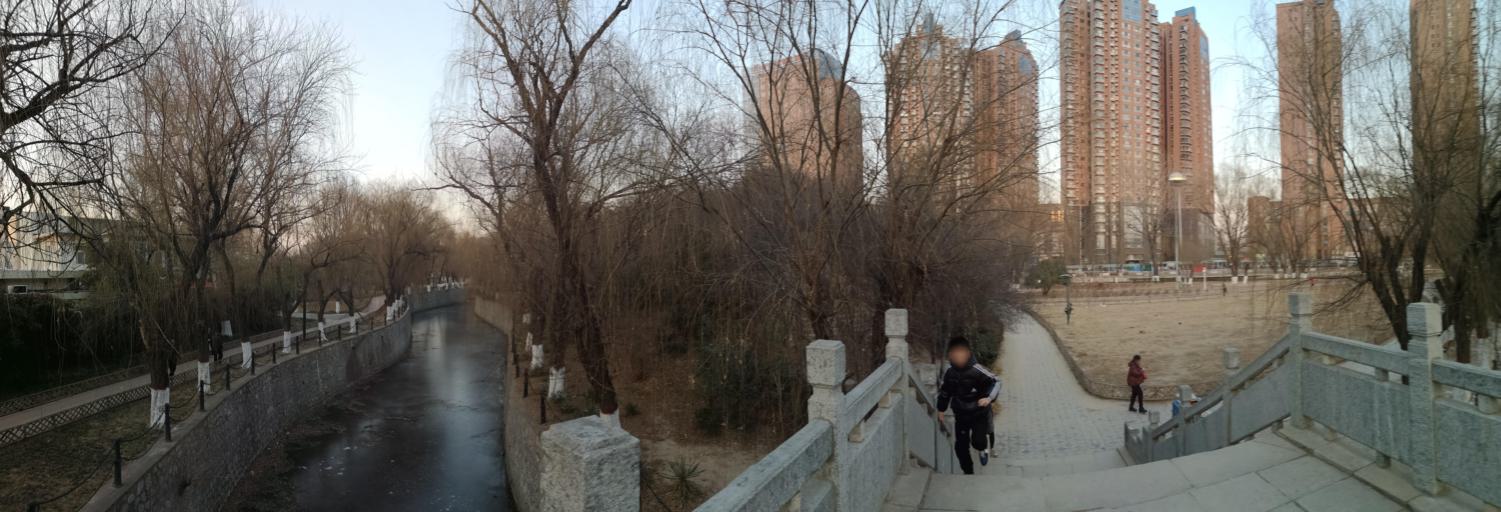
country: CN
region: Henan Sheng
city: Zhongyuanlu
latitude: 35.7730
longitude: 115.0784
